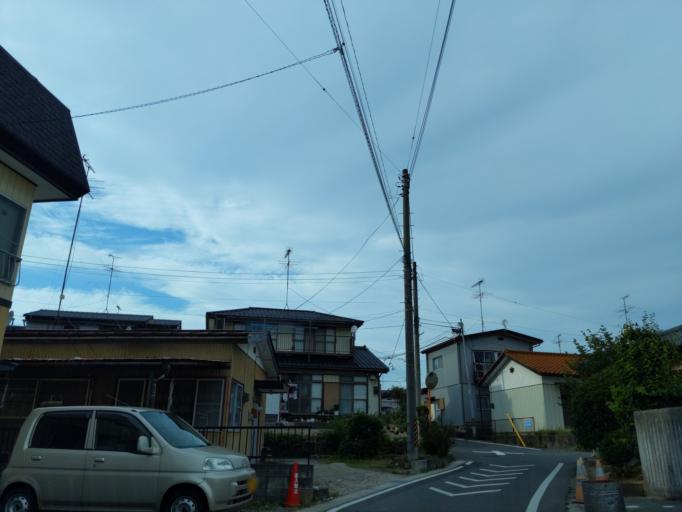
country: JP
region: Fukushima
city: Koriyama
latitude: 37.4131
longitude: 140.3532
